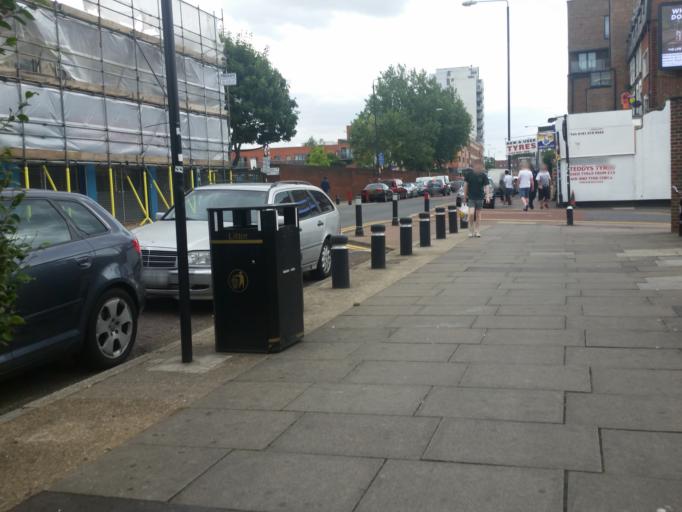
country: GB
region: England
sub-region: Greater London
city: Poplar
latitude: 51.5487
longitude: 0.0052
